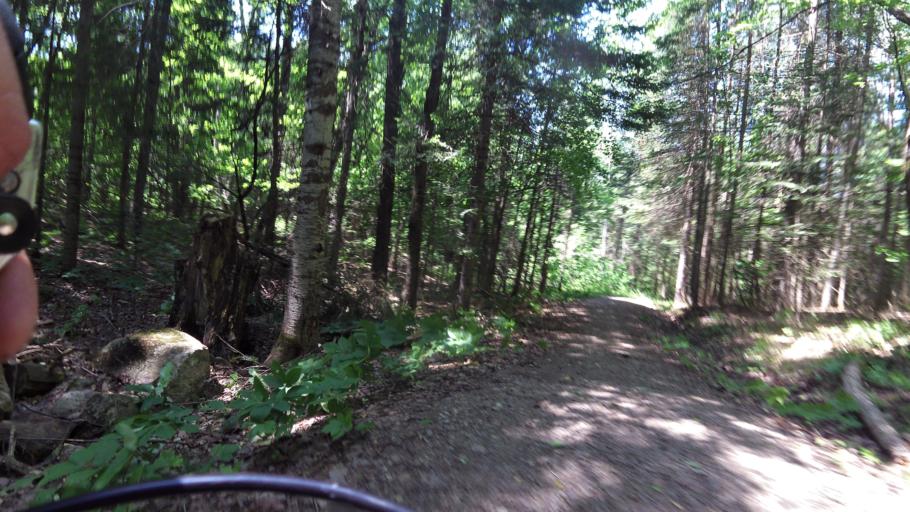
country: CA
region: Quebec
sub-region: Outaouais
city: Wakefield
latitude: 45.6132
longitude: -75.9499
